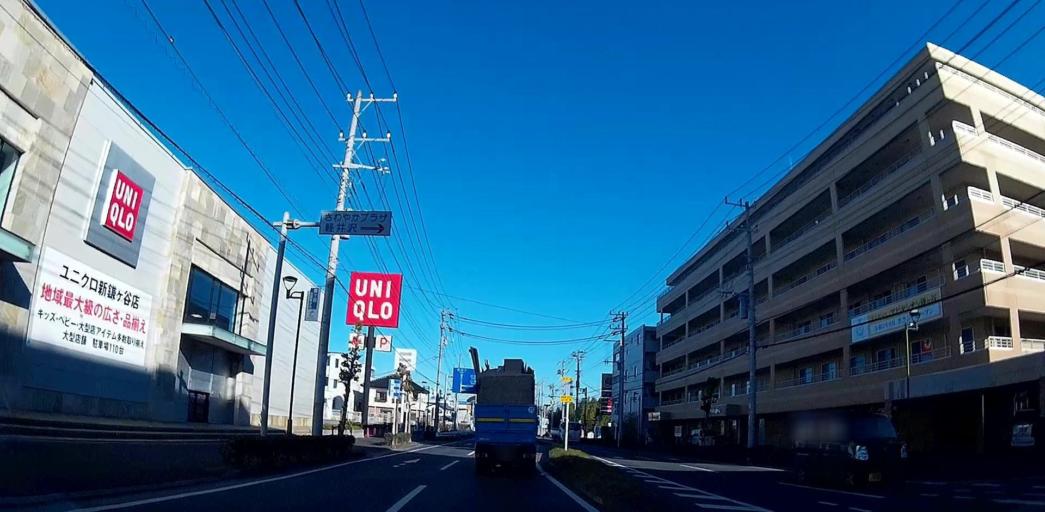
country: JP
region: Chiba
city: Shiroi
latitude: 35.7826
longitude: 140.0025
